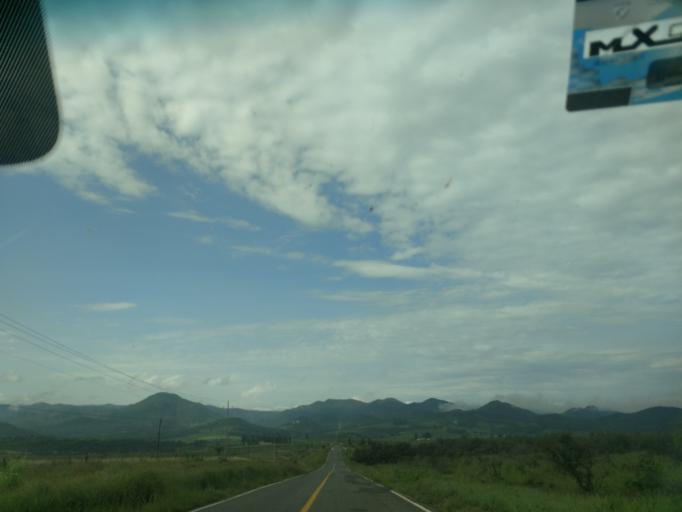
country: MX
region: Jalisco
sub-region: Atengo
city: Soyatlan del Oro
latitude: 20.5337
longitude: -104.3164
